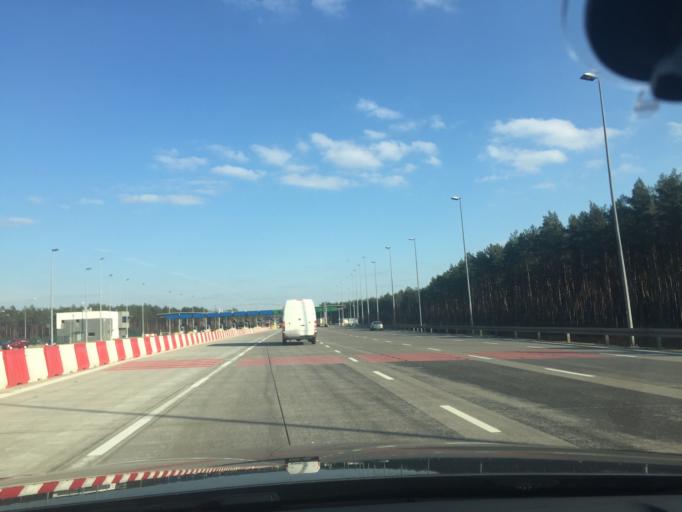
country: PL
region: Lubusz
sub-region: Powiat slubicki
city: Rzepin
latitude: 52.3349
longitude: 14.9001
